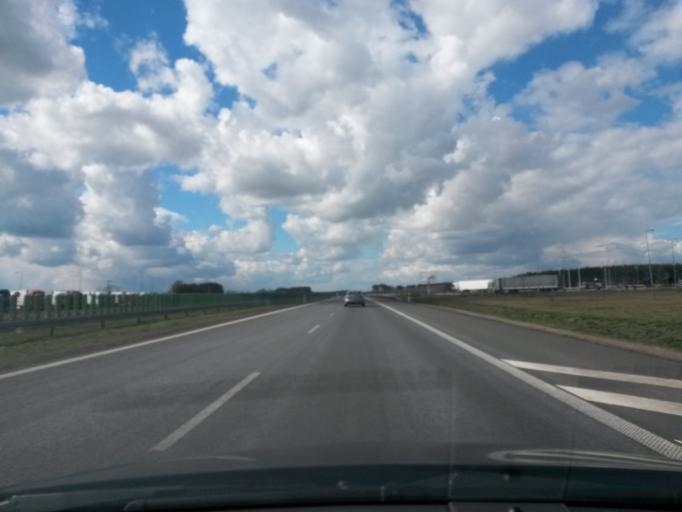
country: PL
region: Greater Poland Voivodeship
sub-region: Powiat kolski
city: Dabie
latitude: 52.0965
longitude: 18.7744
